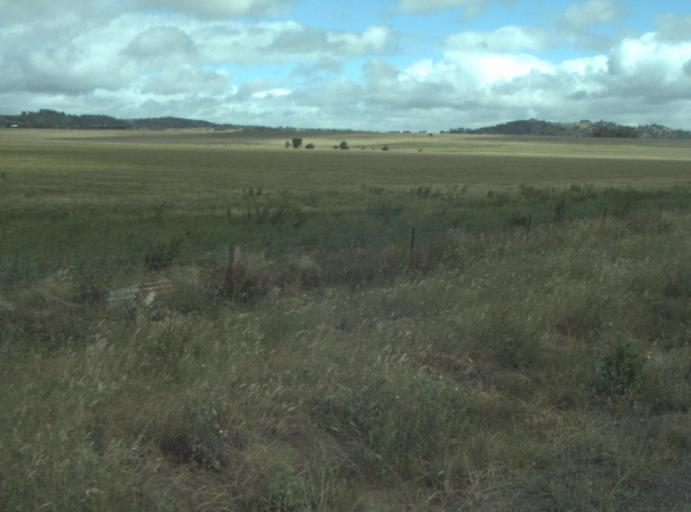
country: AU
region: Victoria
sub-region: Greater Geelong
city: Lara
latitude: -37.9053
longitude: 144.3166
